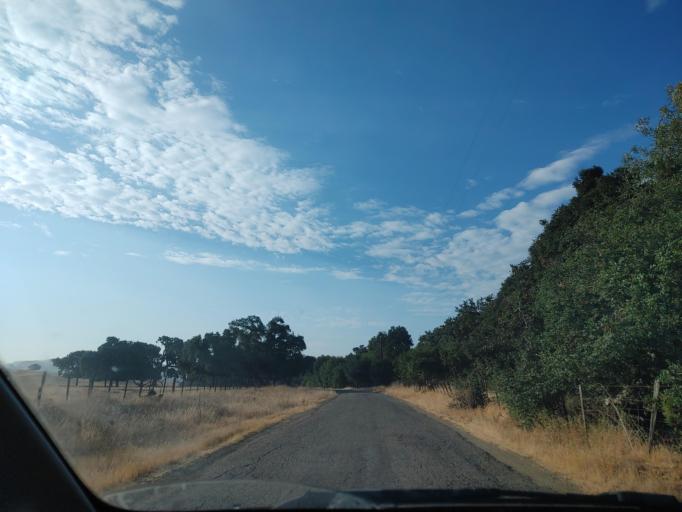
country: US
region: California
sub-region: San Benito County
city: Ridgemark
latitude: 36.7927
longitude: -121.2613
